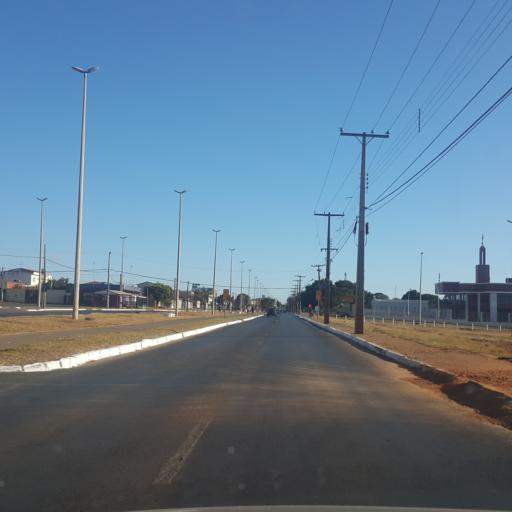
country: BR
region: Federal District
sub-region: Brasilia
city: Brasilia
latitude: -15.8287
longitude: -48.0919
